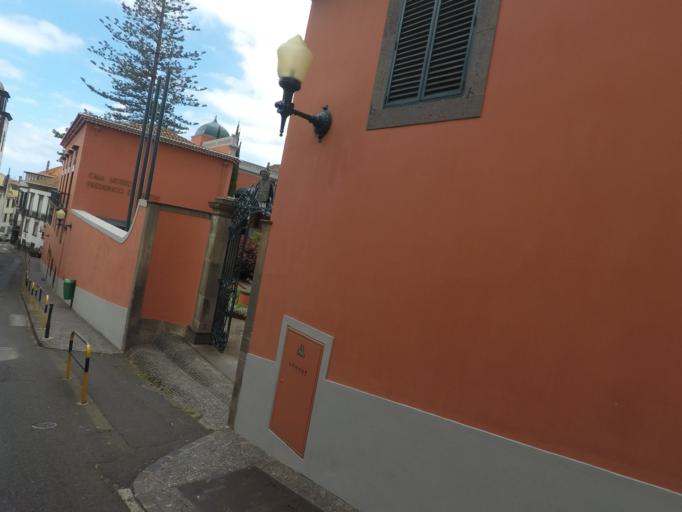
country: PT
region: Madeira
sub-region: Funchal
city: Nossa Senhora do Monte
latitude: 32.6503
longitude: -16.9124
